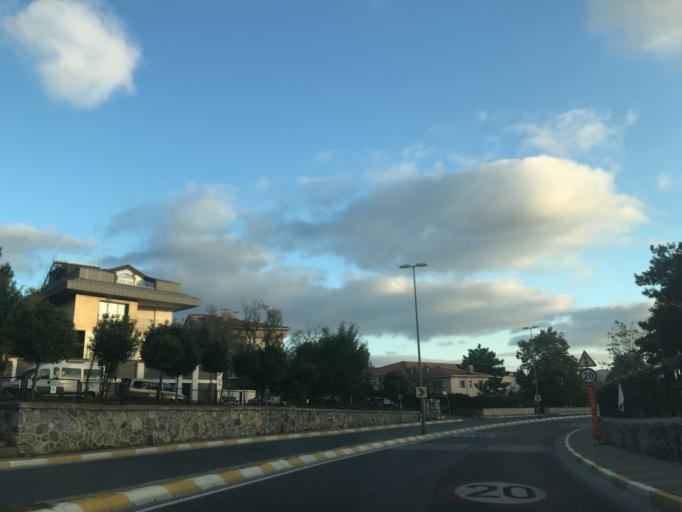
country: TR
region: Istanbul
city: Sisli
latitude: 41.1356
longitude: 29.0397
